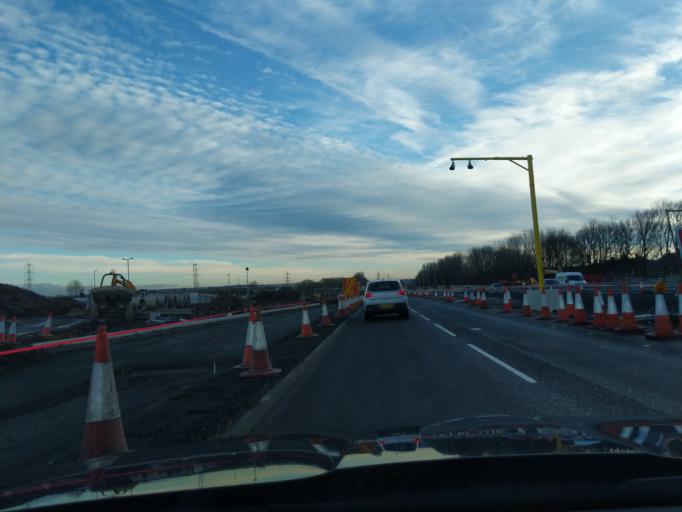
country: GB
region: England
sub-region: South Tyneside
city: Jarrow
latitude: 55.0063
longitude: -1.4945
